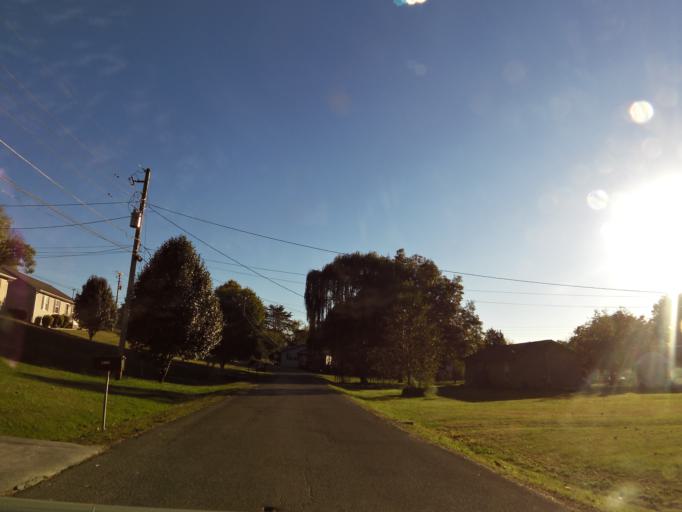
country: US
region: Tennessee
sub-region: Blount County
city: Eagleton Village
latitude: 35.7882
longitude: -83.9522
